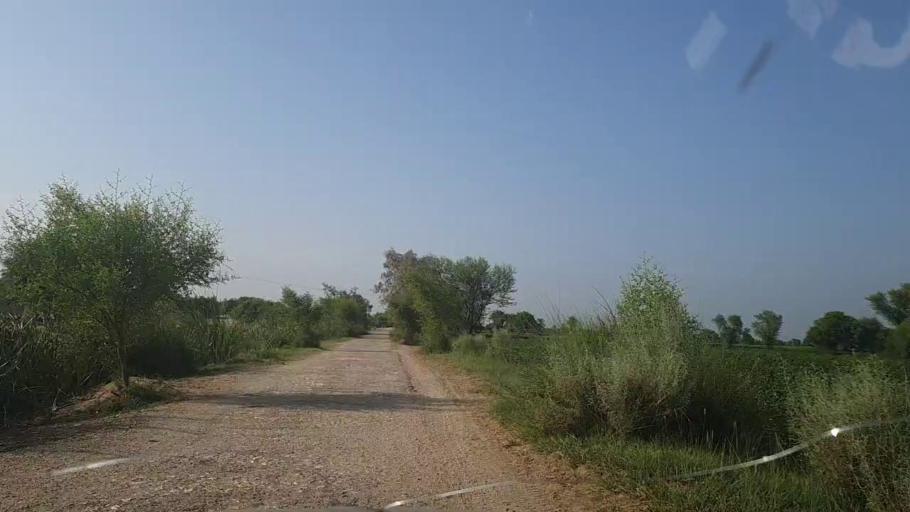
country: PK
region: Sindh
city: Khanpur
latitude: 27.7140
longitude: 69.3320
